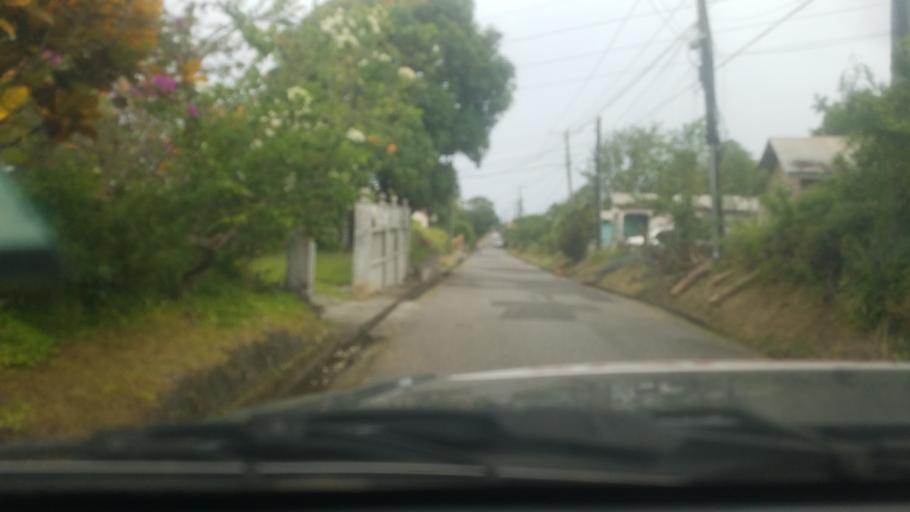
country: LC
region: Laborie Quarter
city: Laborie
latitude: 13.7620
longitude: -60.9799
